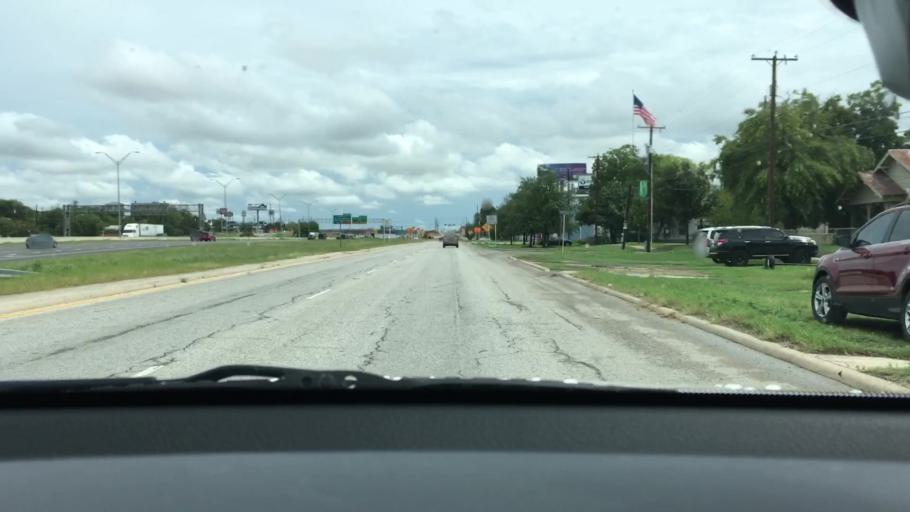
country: US
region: Texas
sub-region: Bexar County
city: San Antonio
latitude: 29.4379
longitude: -98.4678
